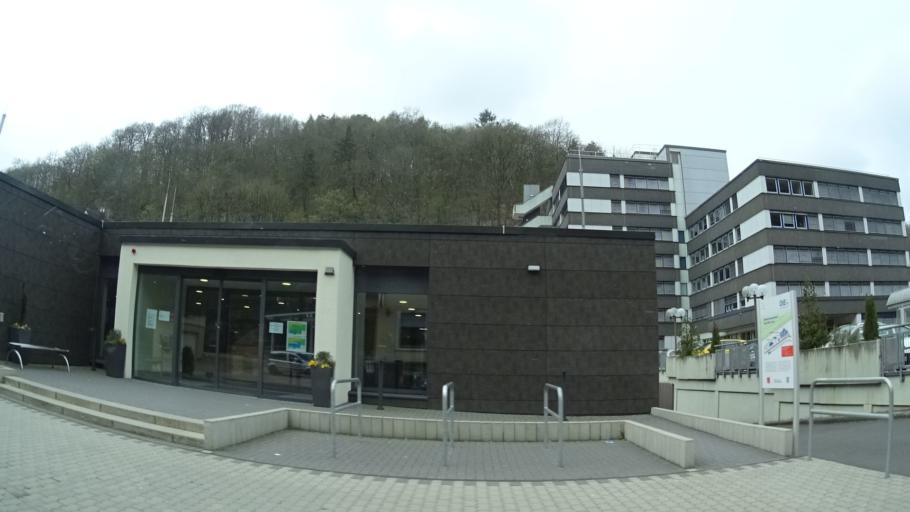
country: DE
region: Rheinland-Pfalz
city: Idar-Oberstein
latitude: 49.7120
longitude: 7.3132
